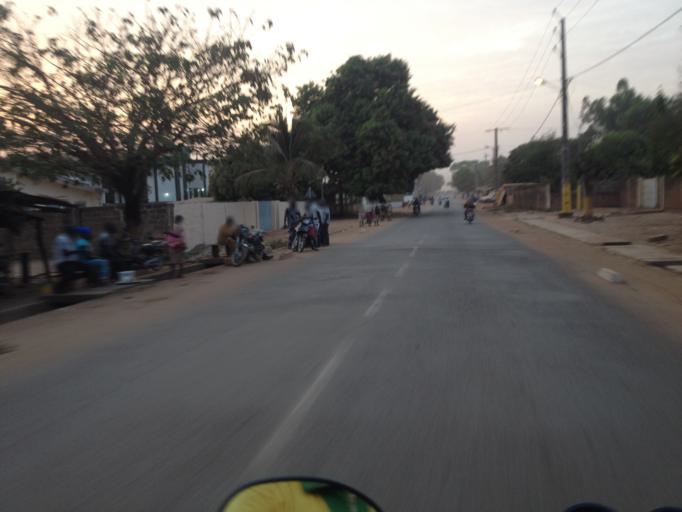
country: BJ
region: Borgou
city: Parakou
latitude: 9.3395
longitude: 2.6333
